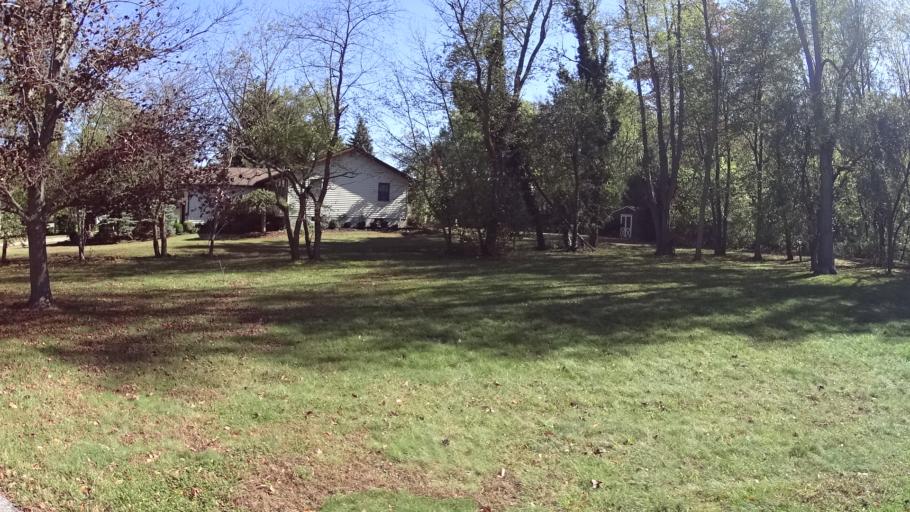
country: US
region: Ohio
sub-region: Lorain County
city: Amherst
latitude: 41.4067
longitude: -82.2025
